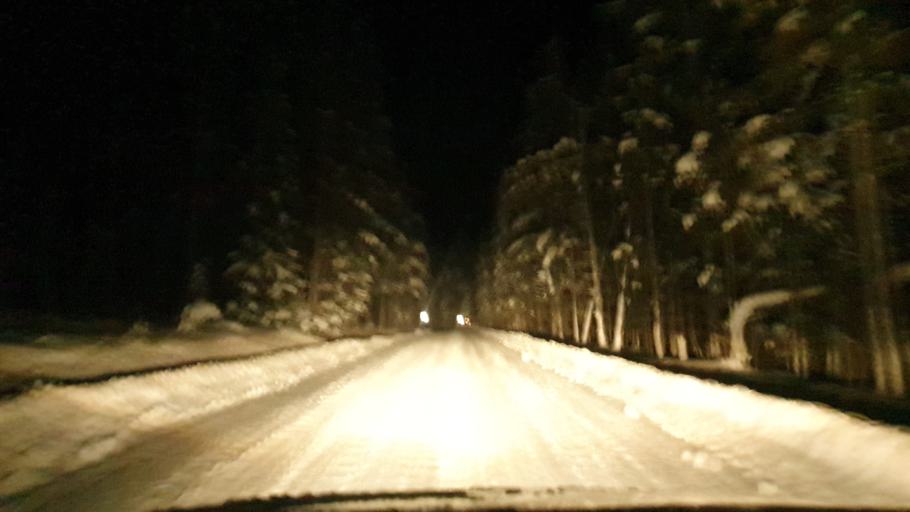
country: EE
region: Vorumaa
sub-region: Antsla vald
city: Vana-Antsla
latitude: 57.9467
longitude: 26.6216
